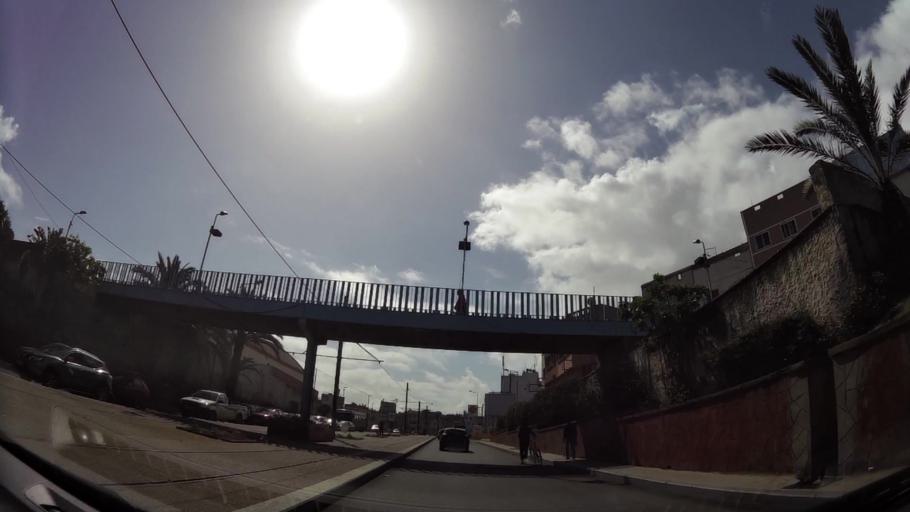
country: MA
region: Grand Casablanca
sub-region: Casablanca
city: Casablanca
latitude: 33.5672
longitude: -7.6100
